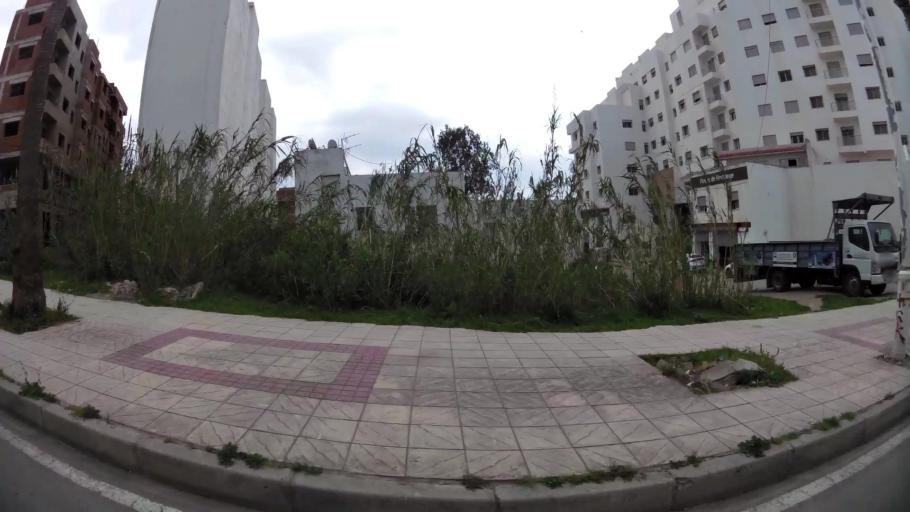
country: MA
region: Tanger-Tetouan
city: Tetouan
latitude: 35.5659
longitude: -5.3812
